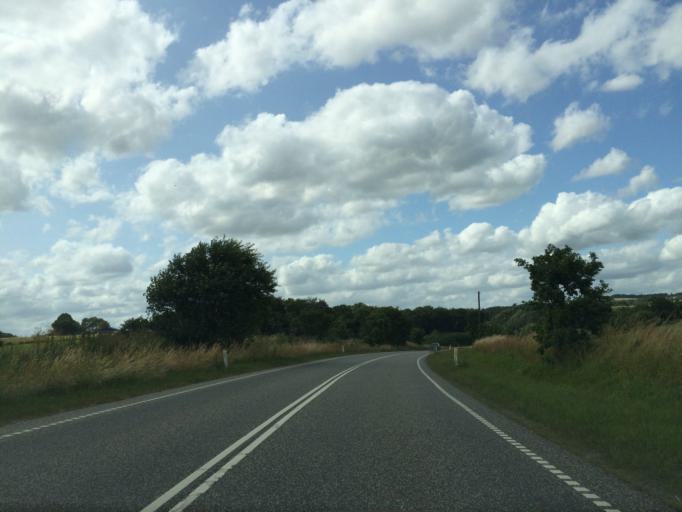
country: DK
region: Central Jutland
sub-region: Skanderborg Kommune
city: Ry
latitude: 56.1606
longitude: 9.8144
